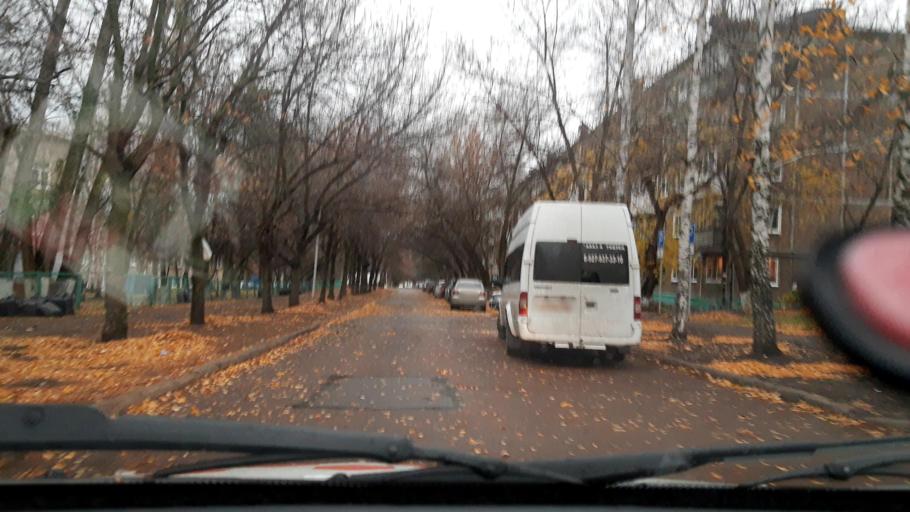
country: RU
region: Bashkortostan
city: Ufa
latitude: 54.7638
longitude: 55.9928
